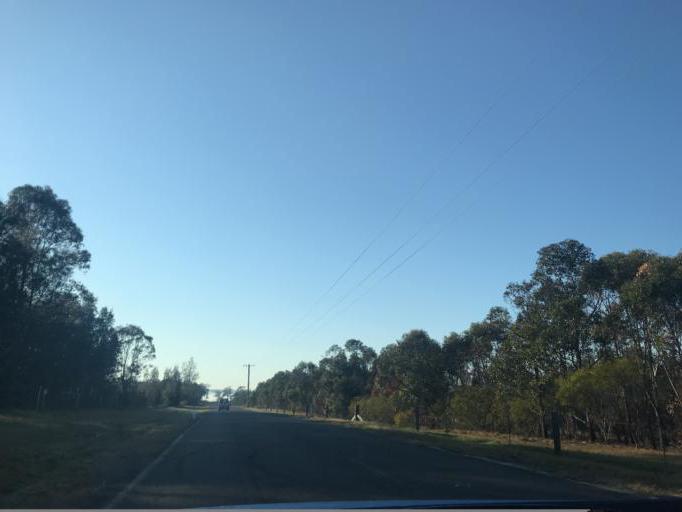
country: AU
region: New South Wales
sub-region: Cessnock
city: Cessnock
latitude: -32.9085
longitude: 151.2916
